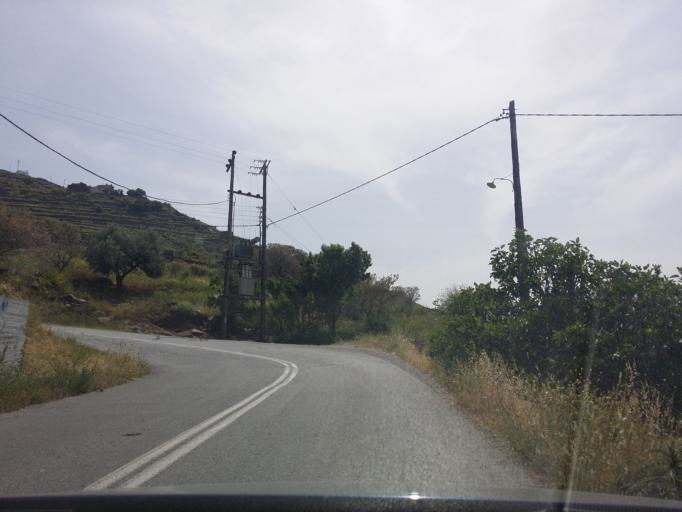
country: GR
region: South Aegean
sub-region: Nomos Kykladon
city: Kea
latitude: 37.6444
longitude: 24.3300
